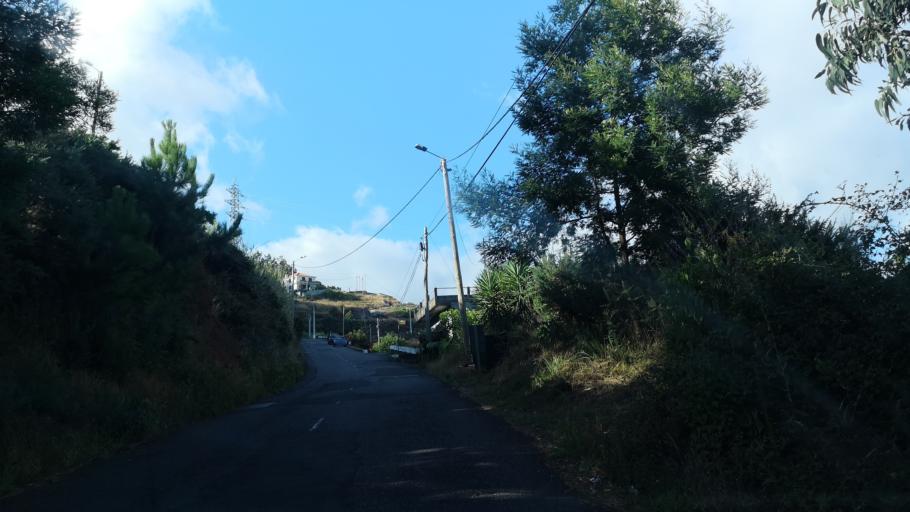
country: PT
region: Madeira
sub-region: Santa Cruz
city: Camacha
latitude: 32.6642
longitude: -16.8371
